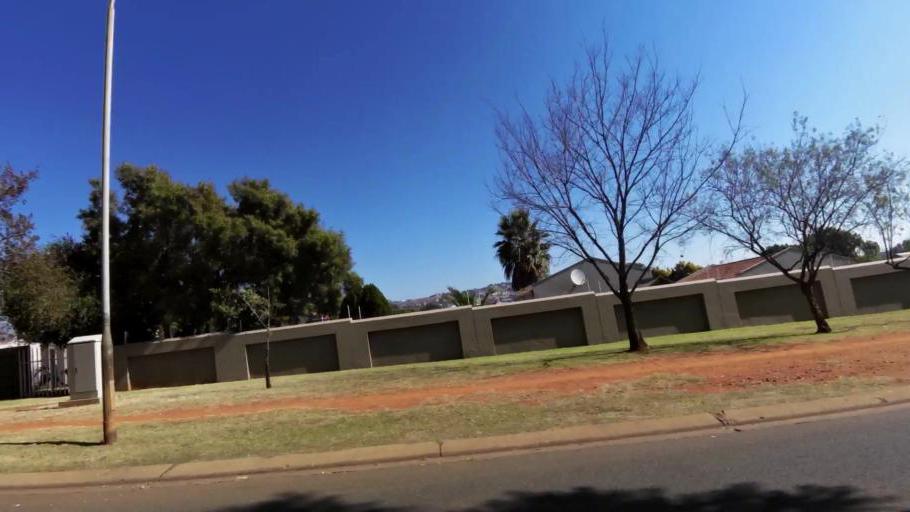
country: ZA
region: Gauteng
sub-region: City of Johannesburg Metropolitan Municipality
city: Roodepoort
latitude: -26.1427
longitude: 27.9361
